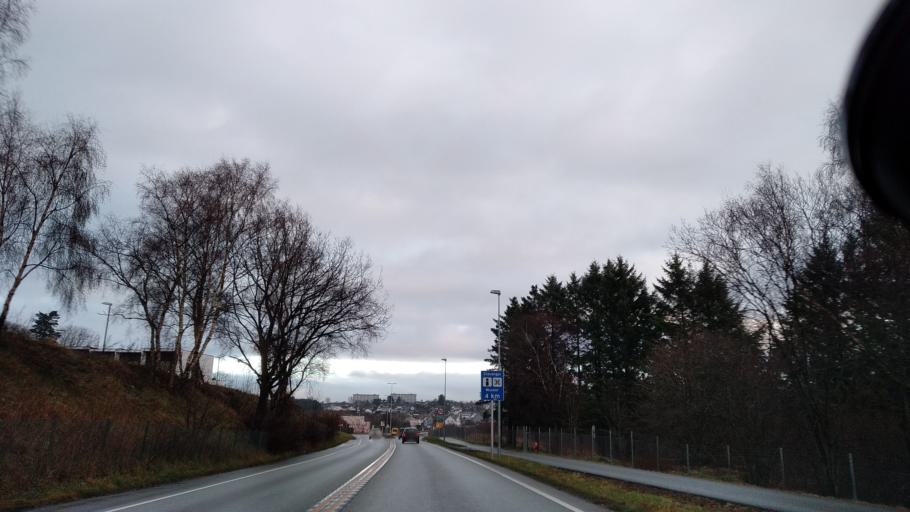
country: NO
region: Rogaland
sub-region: Sola
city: Sola
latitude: 58.9522
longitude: 5.6657
